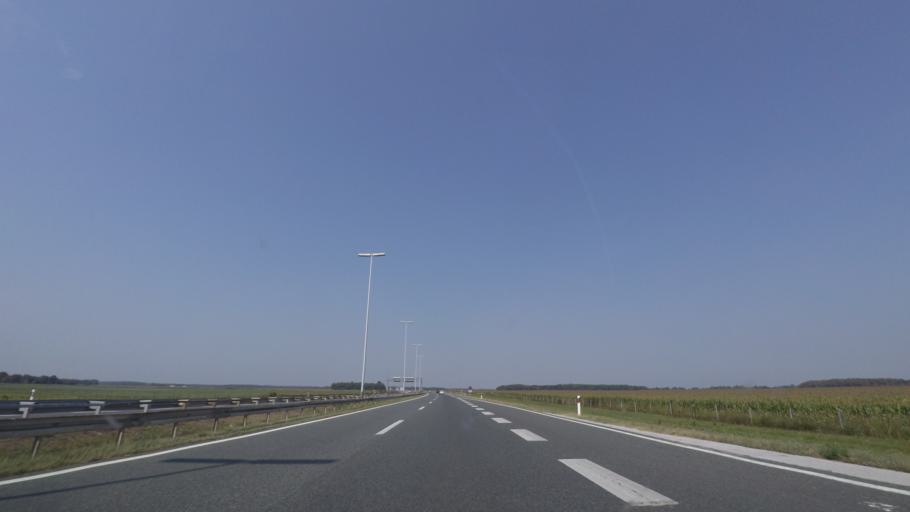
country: HR
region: Sisacko-Moslavacka
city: Osekovo
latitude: 45.5615
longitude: 16.5891
